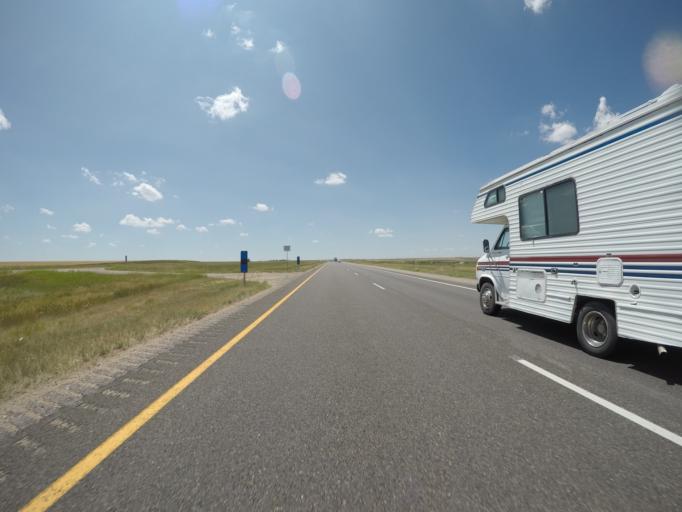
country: US
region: Colorado
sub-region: Lincoln County
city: Hugo
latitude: 39.2861
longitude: -103.1875
